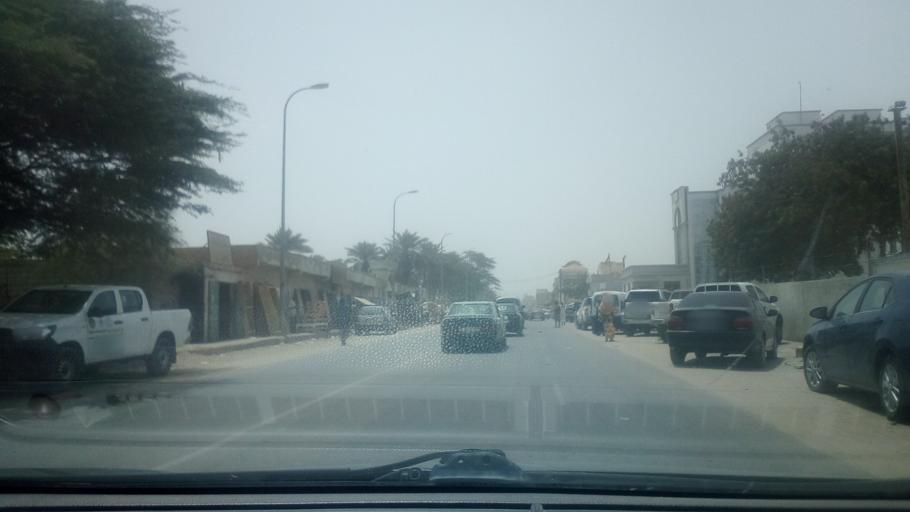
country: MR
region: Nouakchott
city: Nouakchott
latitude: 18.0841
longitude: -15.9906
